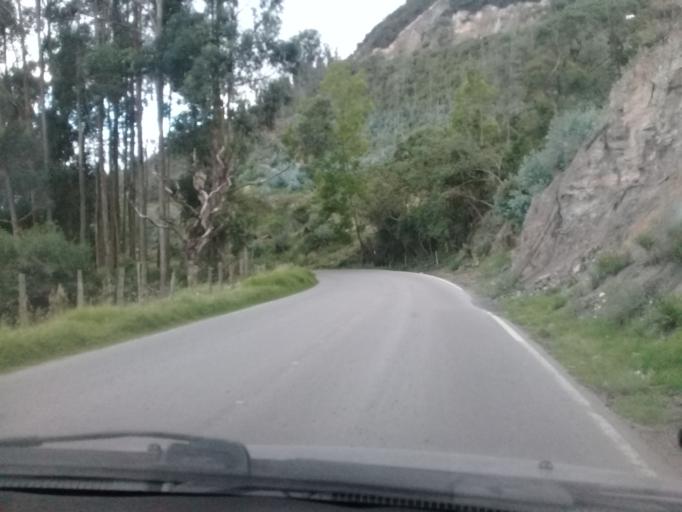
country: CO
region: Cundinamarca
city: Tabio
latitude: 4.9421
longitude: -74.1080
